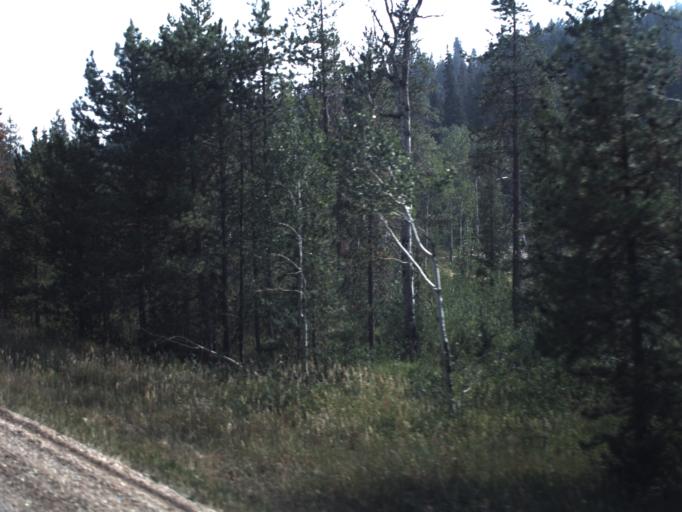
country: US
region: Utah
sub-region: Summit County
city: Francis
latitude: 40.6169
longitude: -111.1321
